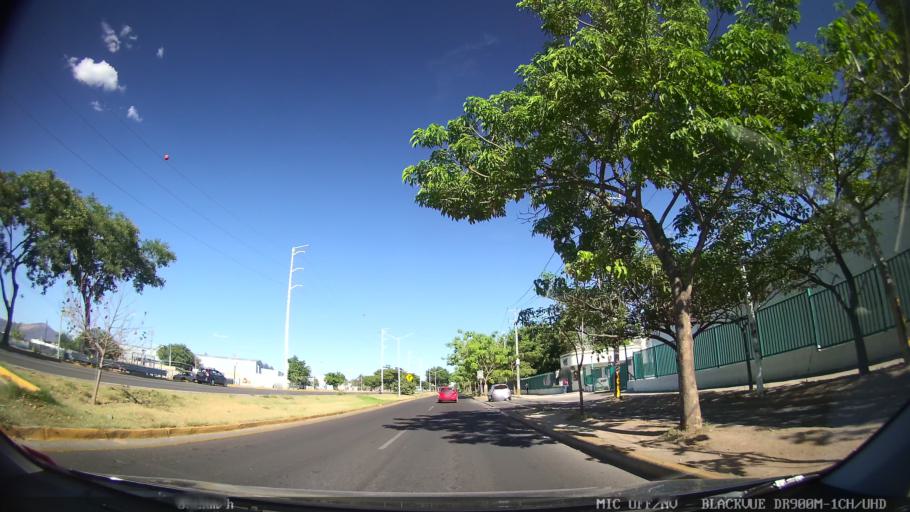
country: MX
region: Jalisco
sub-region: Zapopan
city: Zapopan
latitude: 20.7176
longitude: -103.3106
